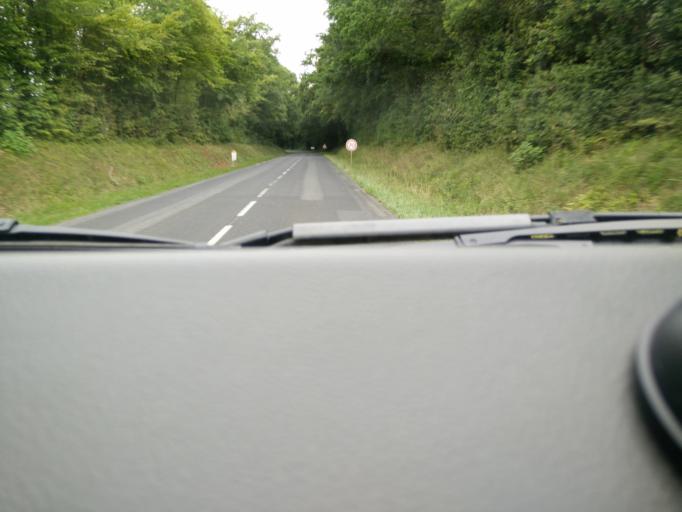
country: FR
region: Lorraine
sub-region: Departement de Meurthe-et-Moselle
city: Montauville
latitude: 48.9354
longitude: 5.8930
